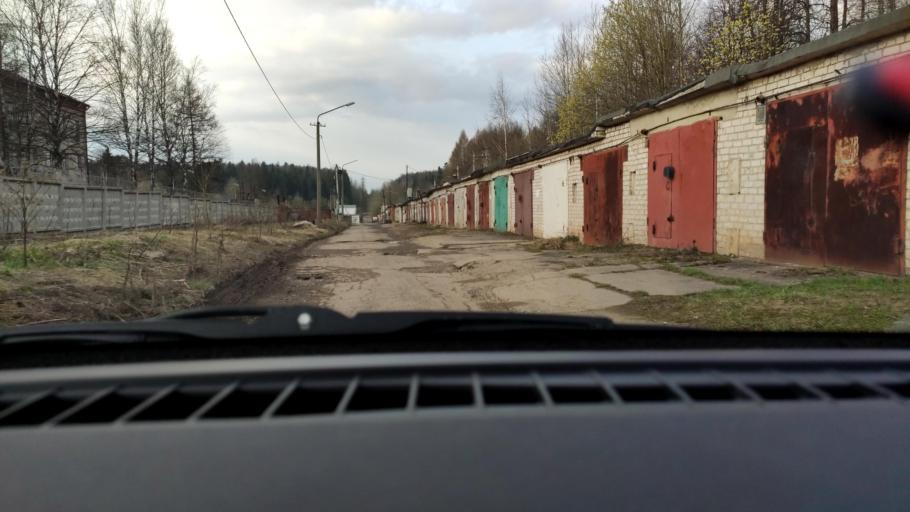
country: RU
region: Perm
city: Froly
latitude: 57.9724
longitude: 56.3211
